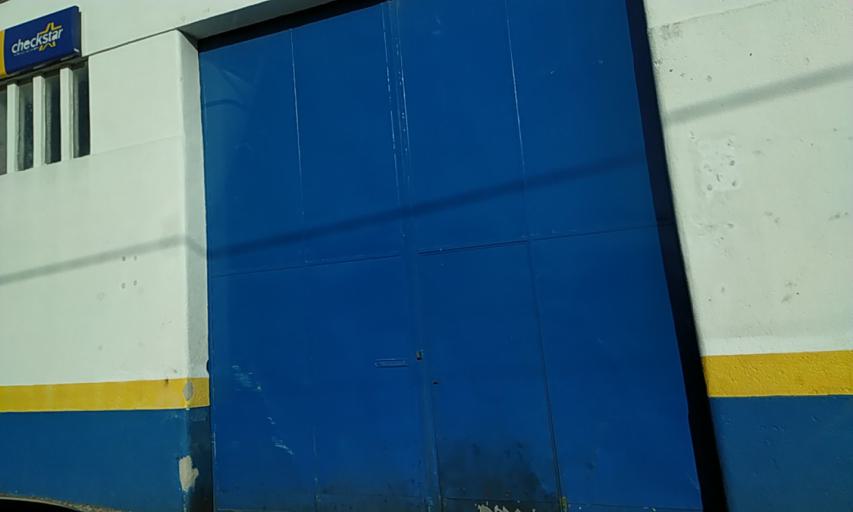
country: PT
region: Santarem
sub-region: Santarem
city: Santarem
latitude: 39.2547
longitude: -8.6820
